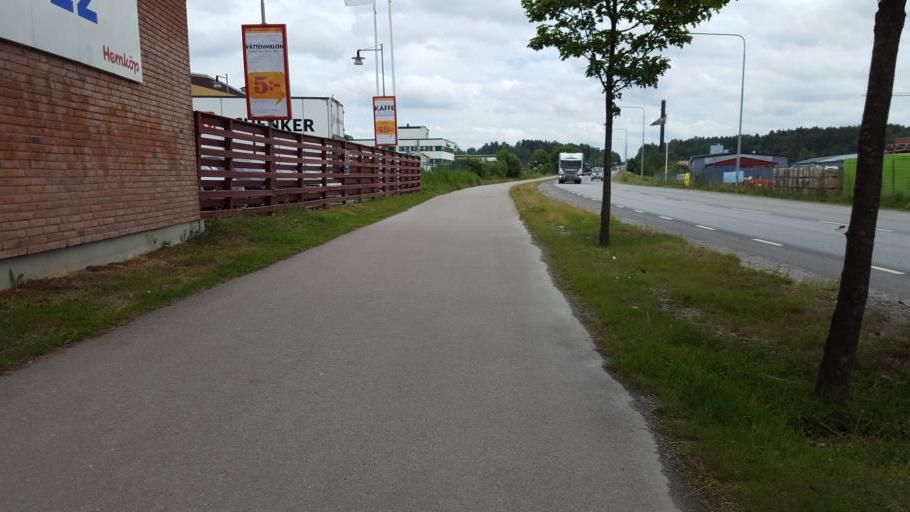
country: SE
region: Stockholm
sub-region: Upplands Vasby Kommun
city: Upplands Vaesby
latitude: 59.5158
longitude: 17.8884
